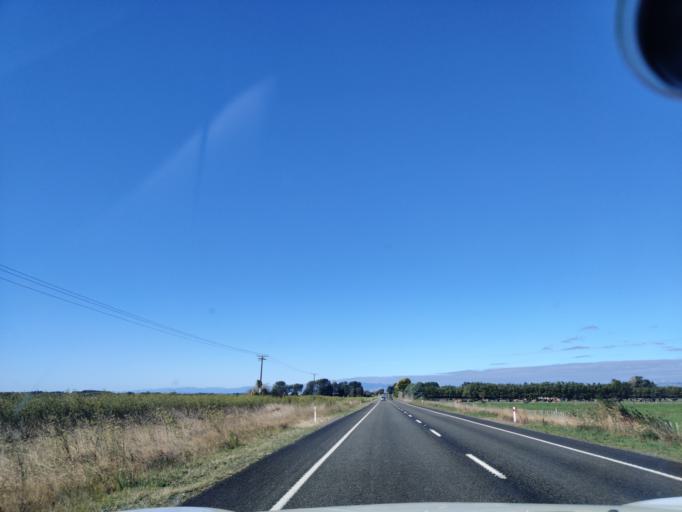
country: NZ
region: Manawatu-Wanganui
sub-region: Palmerston North City
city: Palmerston North
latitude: -40.3893
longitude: 175.5303
